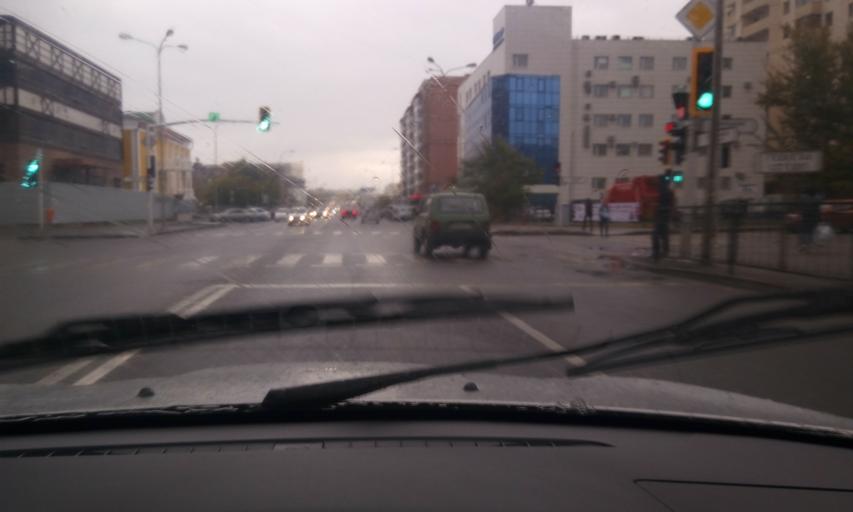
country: KZ
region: Astana Qalasy
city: Astana
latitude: 51.1611
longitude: 71.4585
